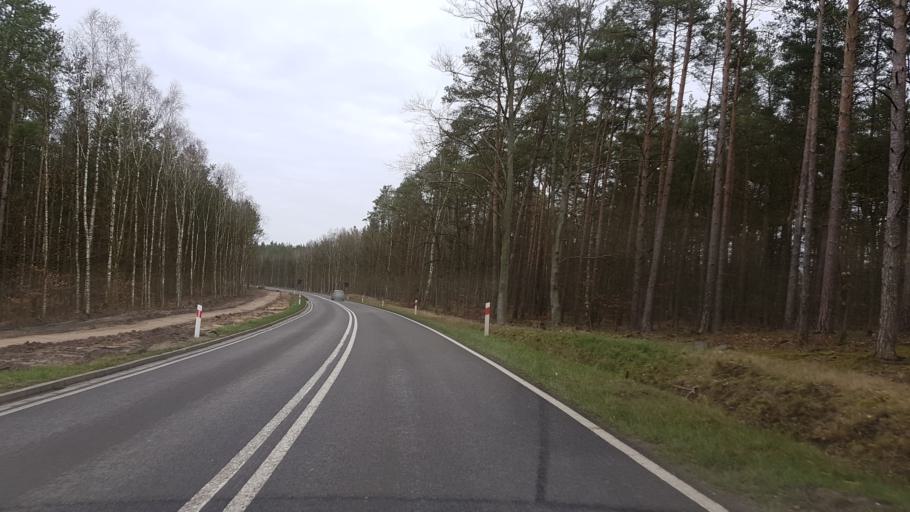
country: PL
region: West Pomeranian Voivodeship
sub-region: Powiat policki
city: Police
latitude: 53.6368
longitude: 14.5054
